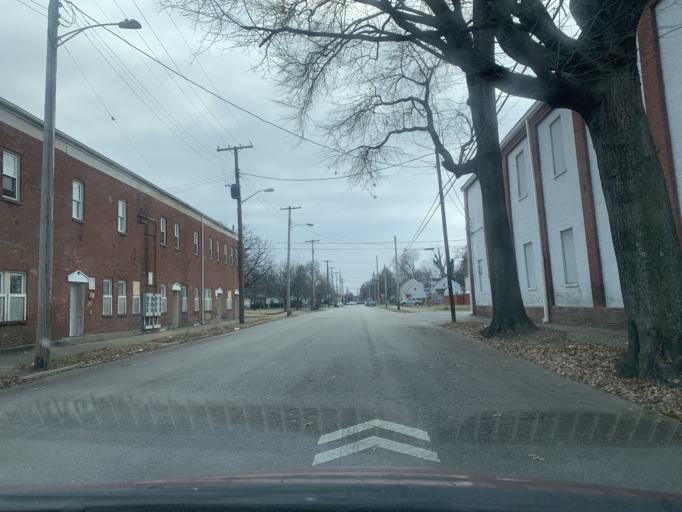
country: US
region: Kentucky
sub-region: Jefferson County
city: Louisville
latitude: 38.2538
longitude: -85.7824
